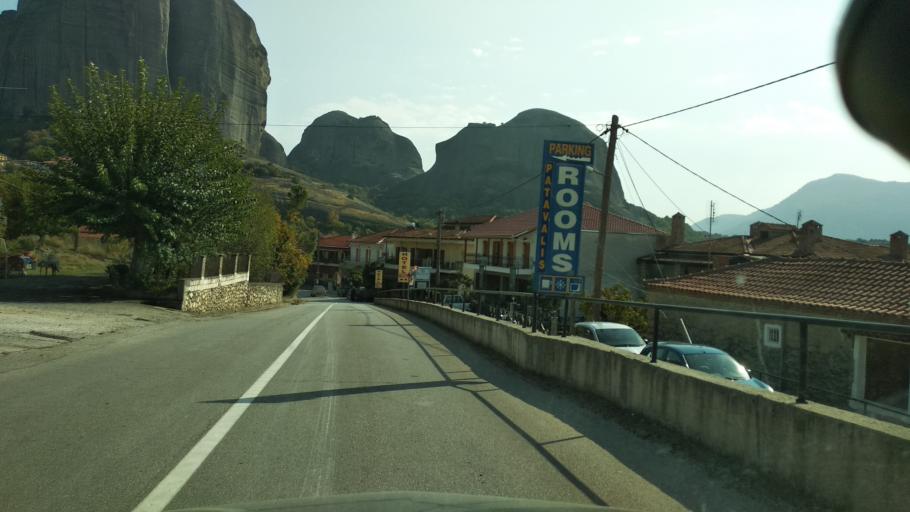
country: GR
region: Thessaly
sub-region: Trikala
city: Kastraki
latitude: 39.7182
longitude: 21.6167
